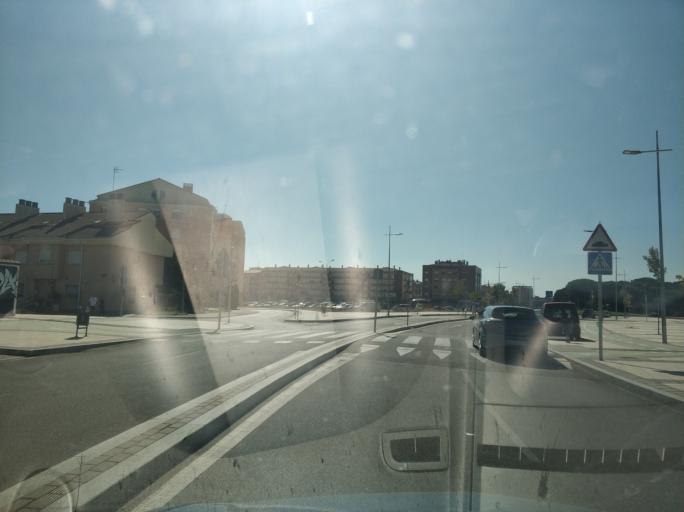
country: ES
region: Castille and Leon
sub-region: Provincia de Burgos
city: Aranda de Duero
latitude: 41.6703
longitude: -3.6937
